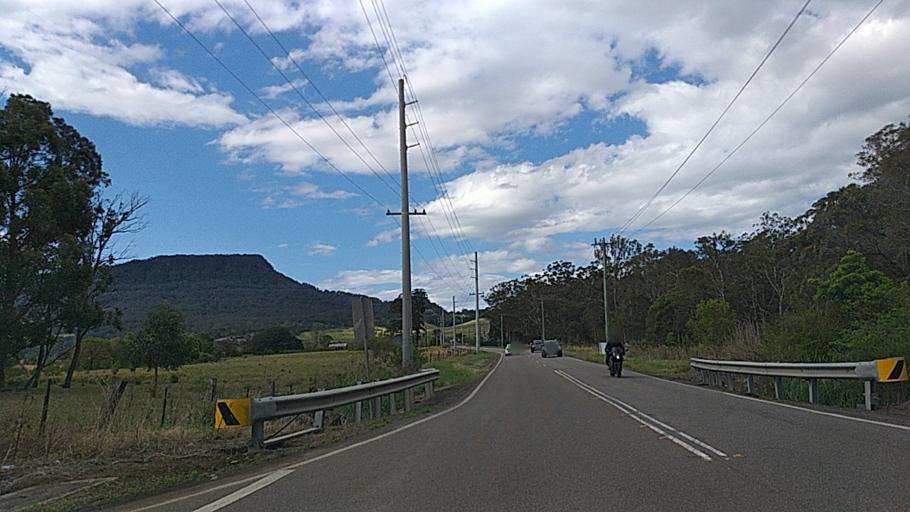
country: AU
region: New South Wales
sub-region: Wollongong
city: Dapto
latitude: -34.4732
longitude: 150.7918
